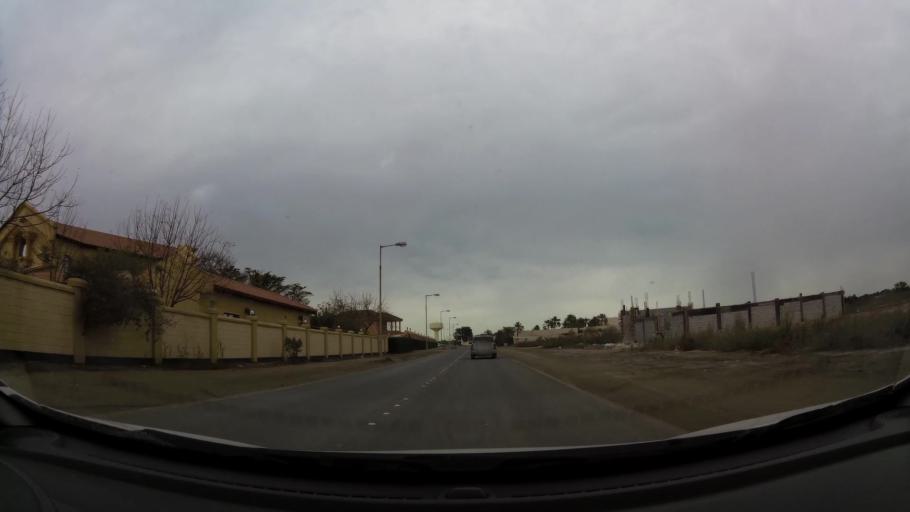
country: BH
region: Central Governorate
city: Madinat Hamad
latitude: 26.1355
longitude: 50.4644
